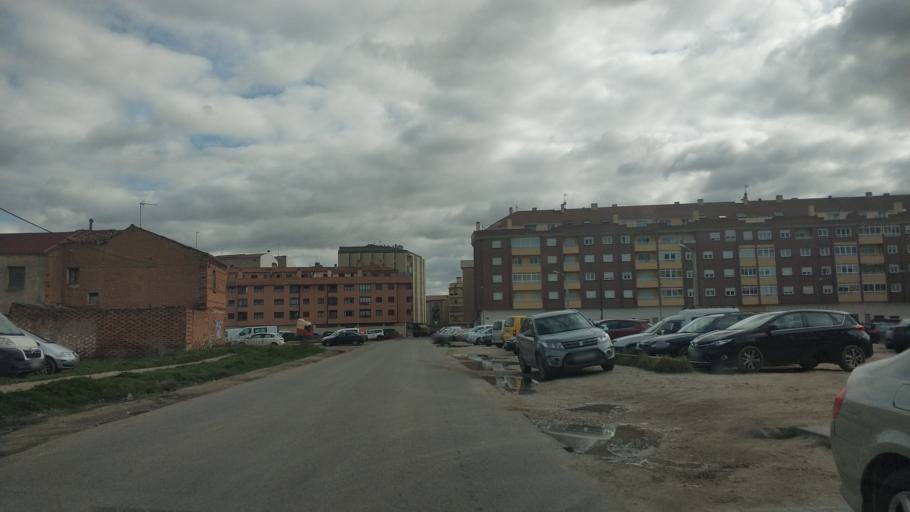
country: ES
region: Castille and Leon
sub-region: Provincia de Burgos
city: Aranda de Duero
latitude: 41.6739
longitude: -3.6823
